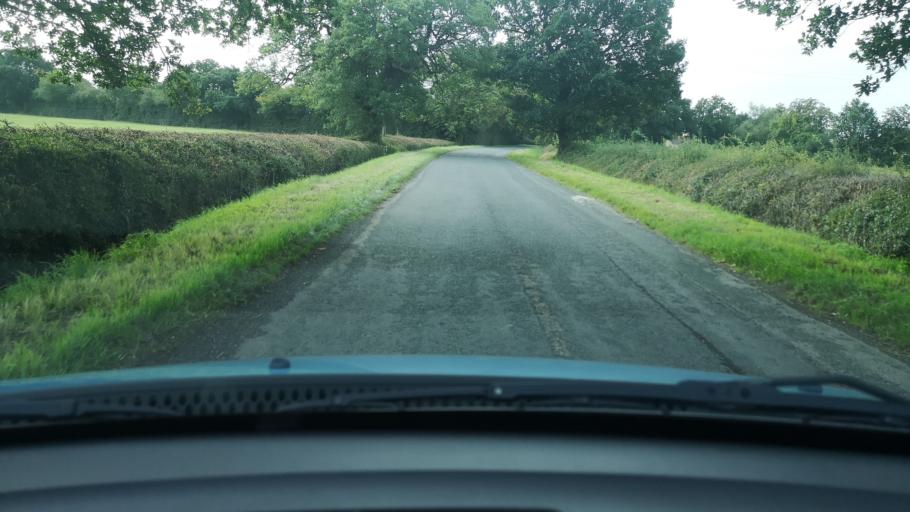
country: GB
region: England
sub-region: East Riding of Yorkshire
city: Pollington
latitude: 53.6463
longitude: -1.0356
